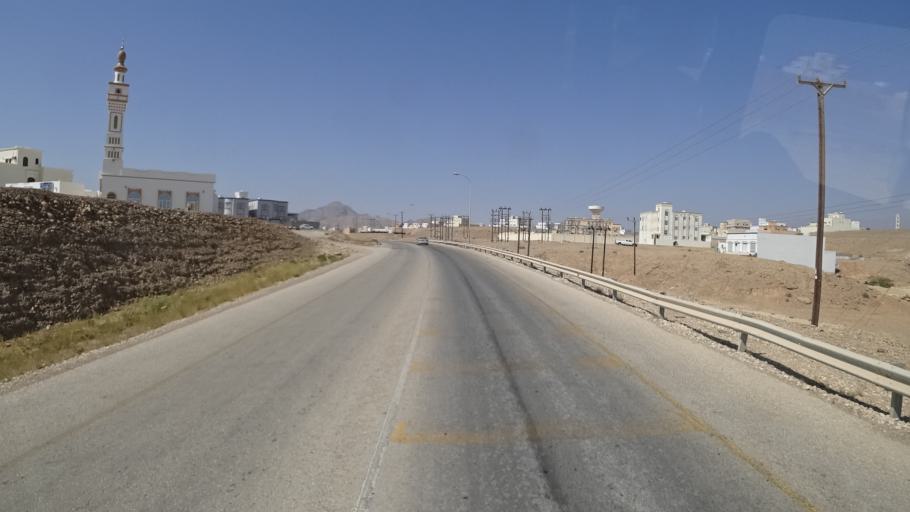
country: OM
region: Ash Sharqiyah
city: Sur
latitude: 22.5581
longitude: 59.4999
